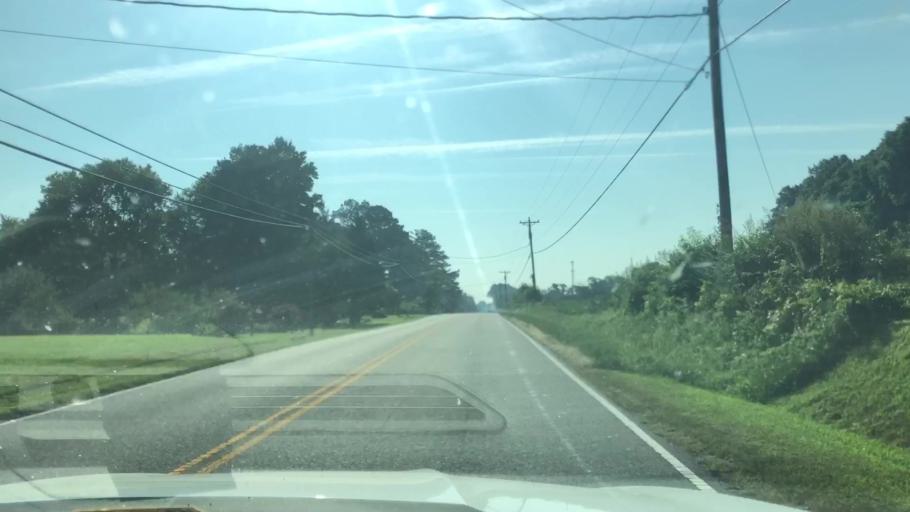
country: US
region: Virginia
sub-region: Richmond County
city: Warsaw
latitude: 37.8953
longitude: -76.6488
